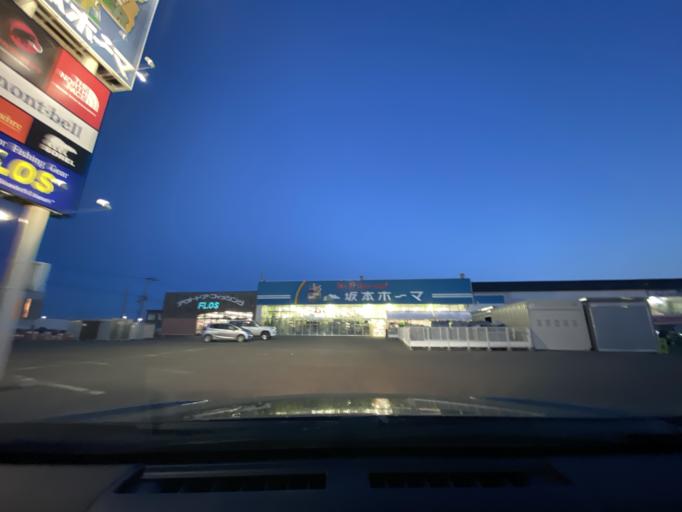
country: JP
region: Hokkaido
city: Kitami
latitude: 43.7977
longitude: 143.8529
